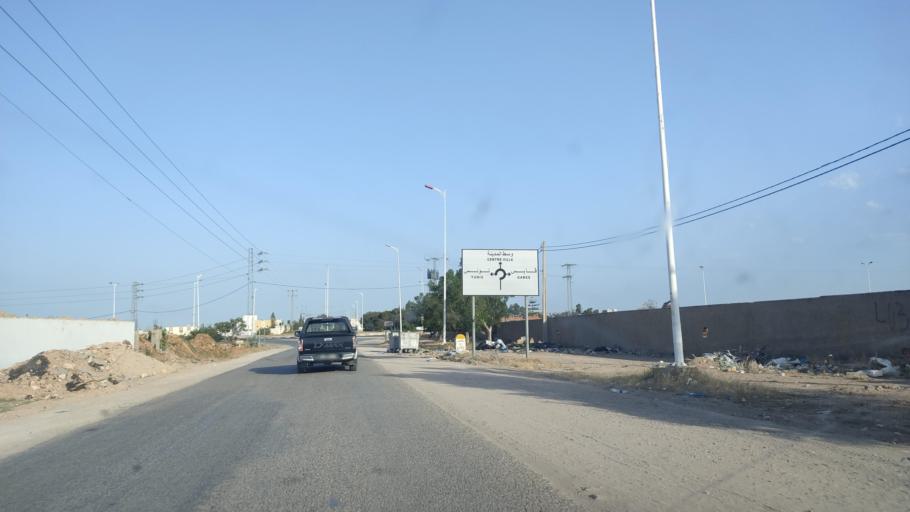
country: TN
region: Safaqis
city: Sfax
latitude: 34.7977
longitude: 10.6779
